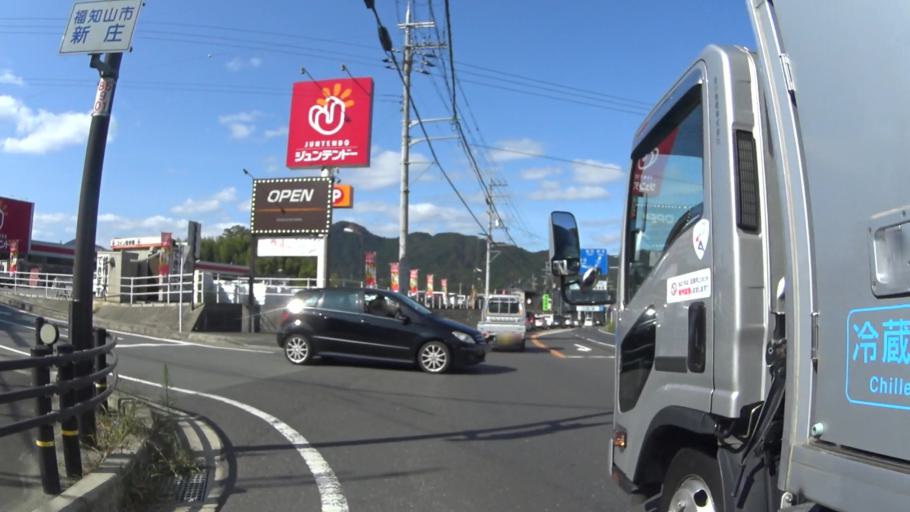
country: JP
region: Kyoto
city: Fukuchiyama
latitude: 35.3043
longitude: 135.1047
